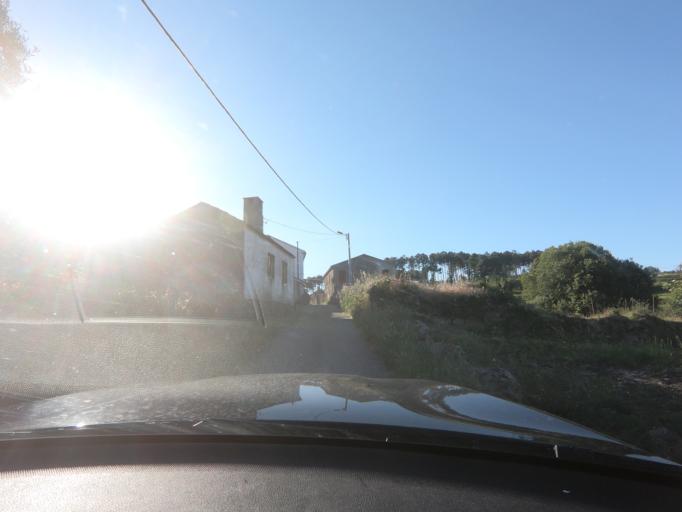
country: PT
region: Vila Real
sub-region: Vila Real
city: Vila Real
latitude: 41.3151
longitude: -7.6841
